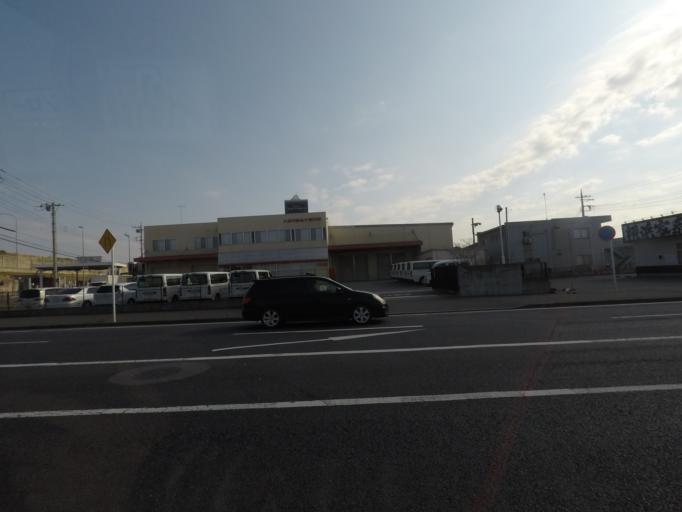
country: JP
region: Chiba
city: Narita
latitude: 35.7455
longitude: 140.3139
